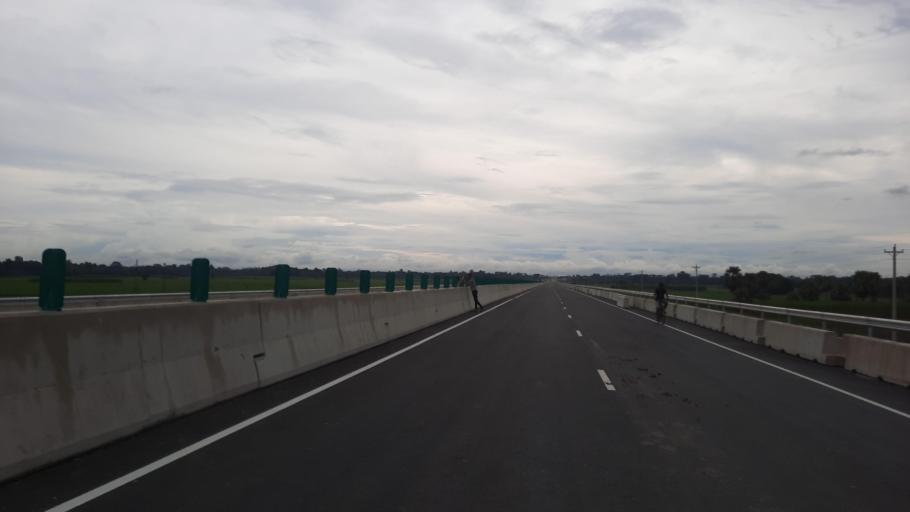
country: BD
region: Khulna
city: Kalia
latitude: 23.2051
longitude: 89.7095
